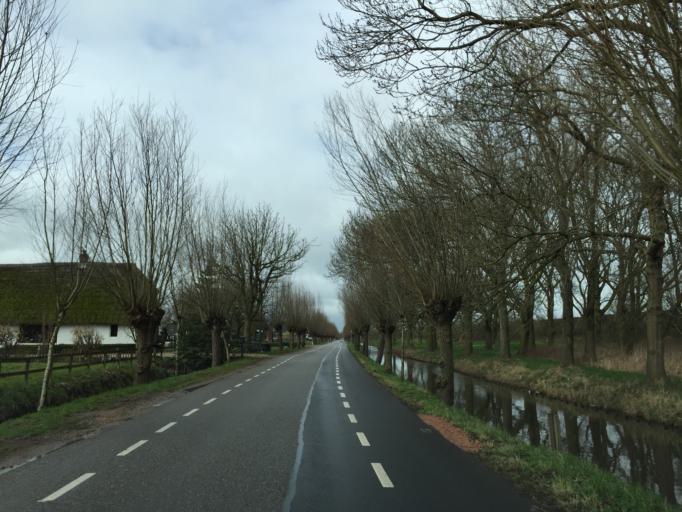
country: NL
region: Utrecht
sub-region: Gemeente IJsselstein
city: IJsselstein
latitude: 52.0731
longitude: 5.0234
